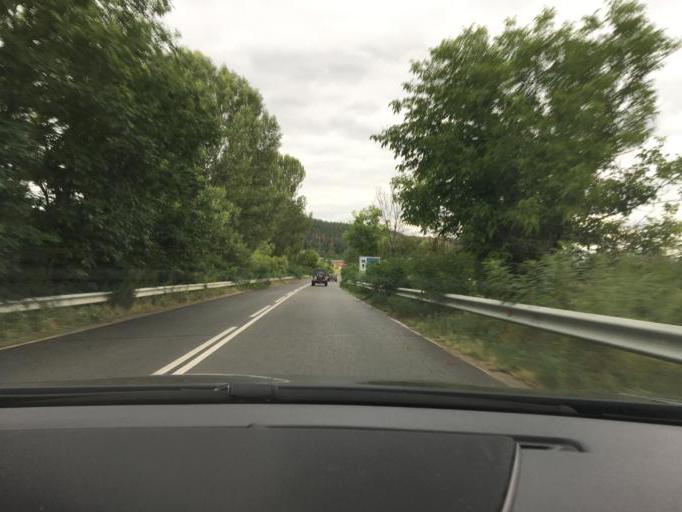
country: BG
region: Kyustendil
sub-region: Obshtina Kyustendil
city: Kyustendil
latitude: 42.2573
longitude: 22.8464
